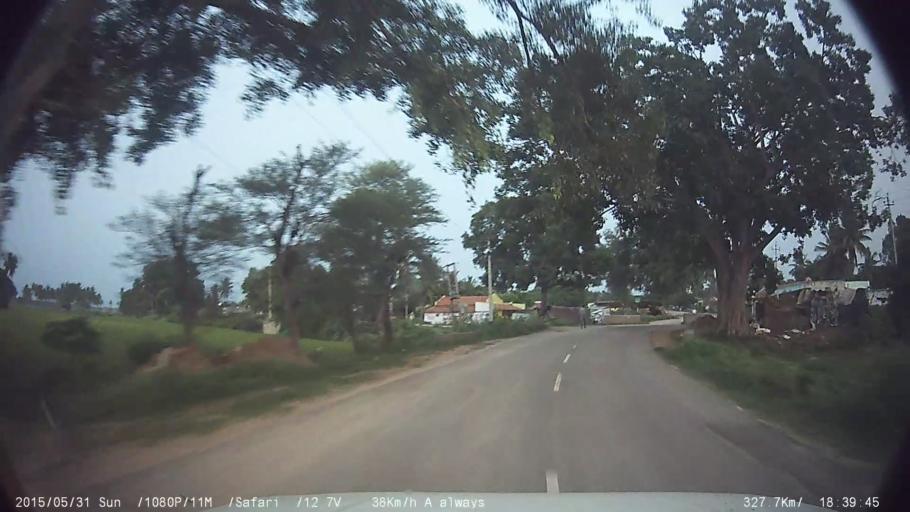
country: IN
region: Karnataka
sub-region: Mysore
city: Nanjangud
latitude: 12.1481
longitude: 76.7830
